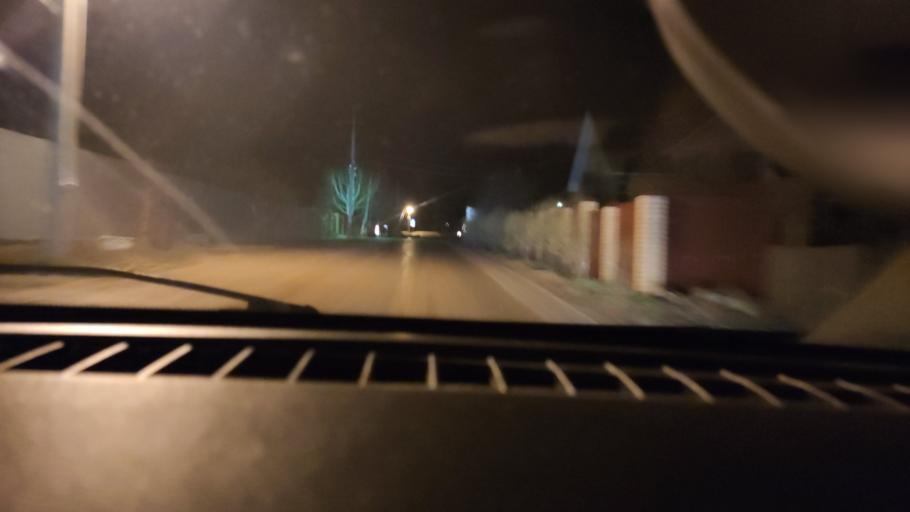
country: RU
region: Perm
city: Ferma
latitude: 57.9379
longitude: 56.3263
